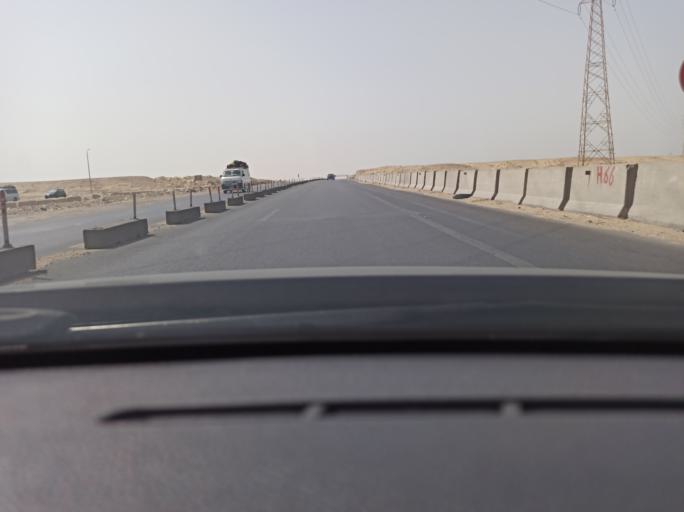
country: EG
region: Muhafazat al Fayyum
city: Al Wasitah
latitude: 29.2957
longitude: 31.2765
